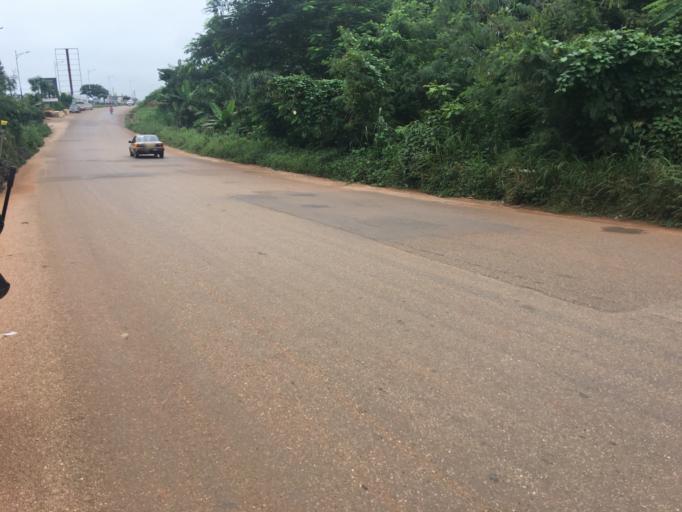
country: GH
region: Western
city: Bibiani
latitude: 6.8069
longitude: -2.5106
